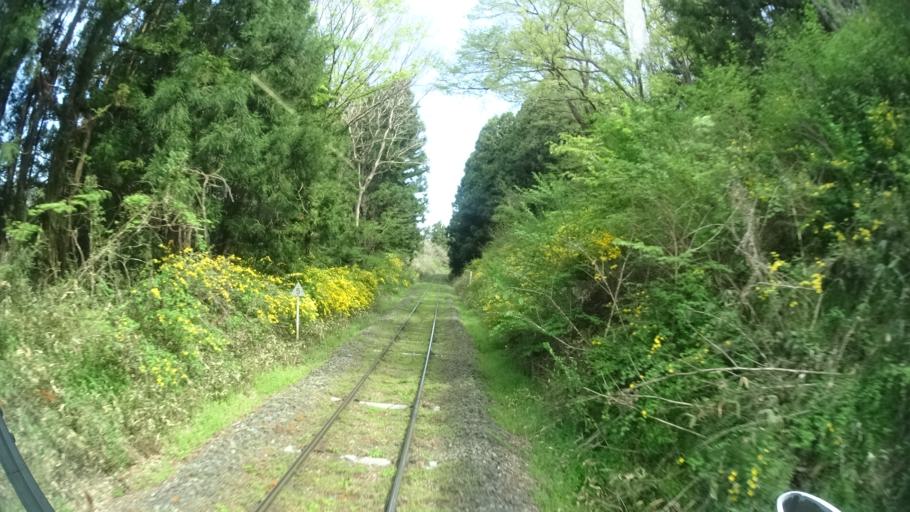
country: JP
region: Iwate
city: Ichinoseki
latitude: 38.9922
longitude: 141.2562
